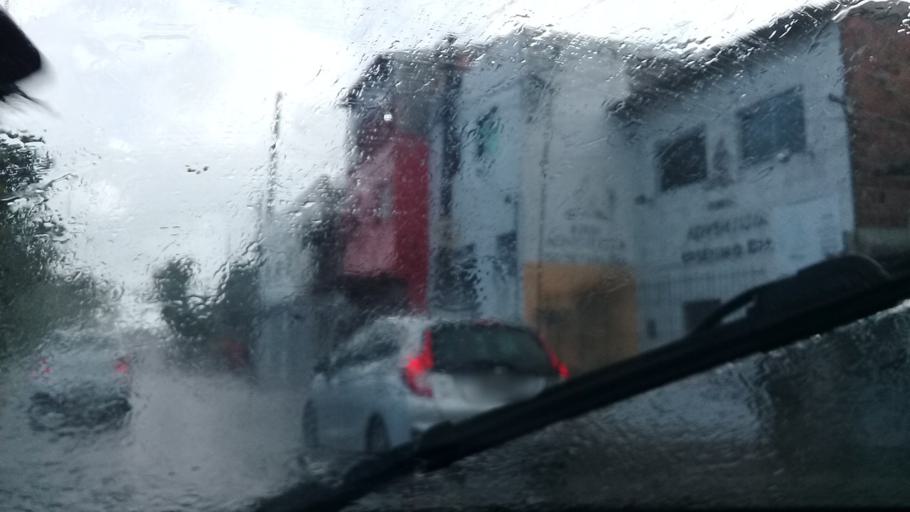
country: BR
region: Pernambuco
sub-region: Recife
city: Recife
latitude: -8.1287
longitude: -34.9104
